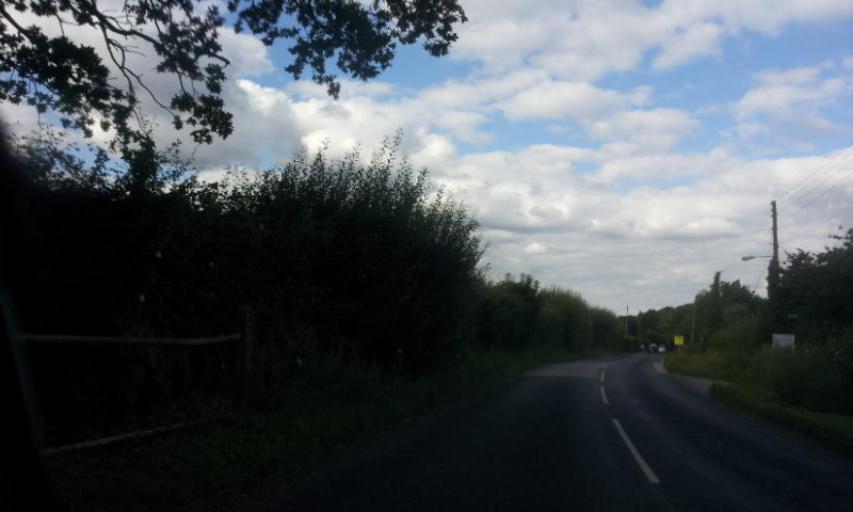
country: GB
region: England
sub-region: Kent
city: Staplehurst
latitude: 51.1765
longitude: 0.5811
